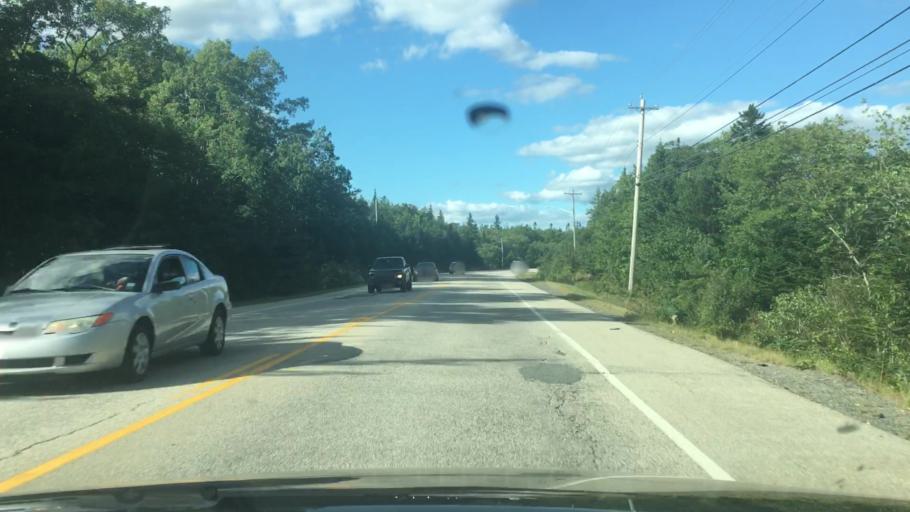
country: CA
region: Nova Scotia
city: Halifax
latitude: 44.6137
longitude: -63.6698
